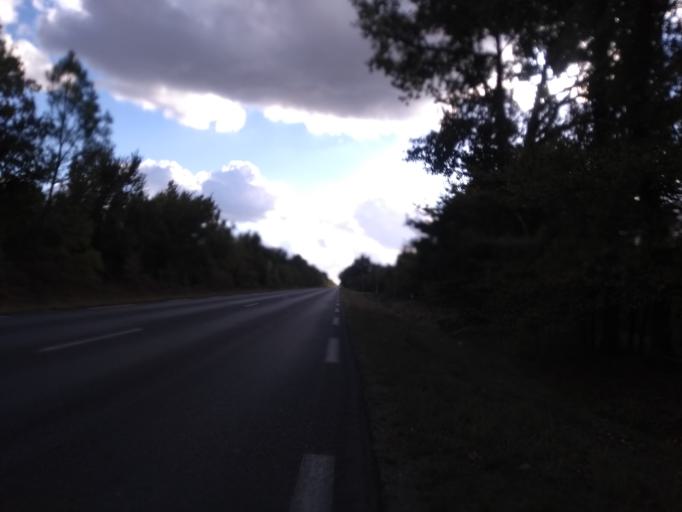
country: FR
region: Aquitaine
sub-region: Departement de la Gironde
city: Saint-Aubin-de-Medoc
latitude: 44.6779
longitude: -0.7269
